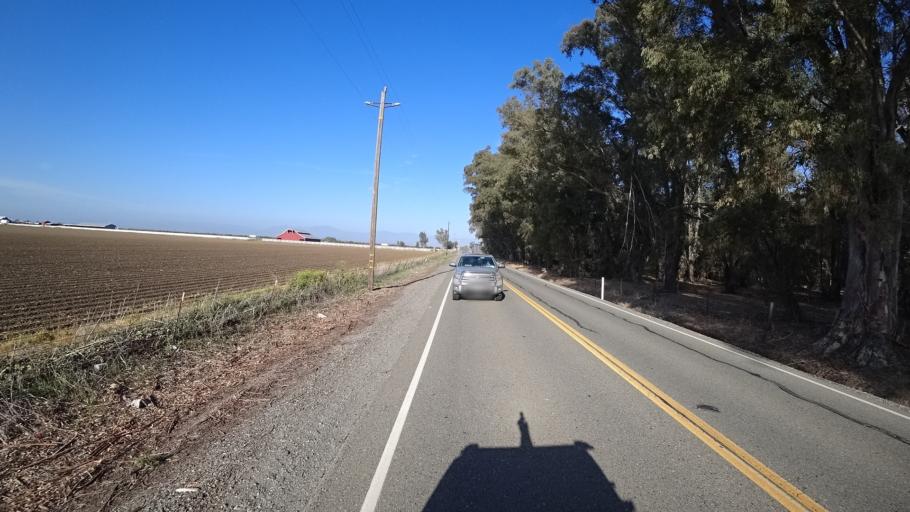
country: US
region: California
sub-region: Glenn County
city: Willows
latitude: 39.5823
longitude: -122.2030
